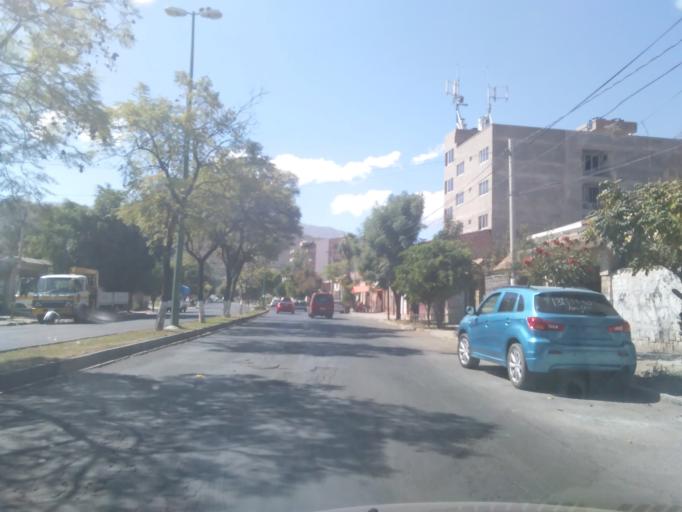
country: BO
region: Cochabamba
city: Cochabamba
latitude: -17.3962
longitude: -66.1439
